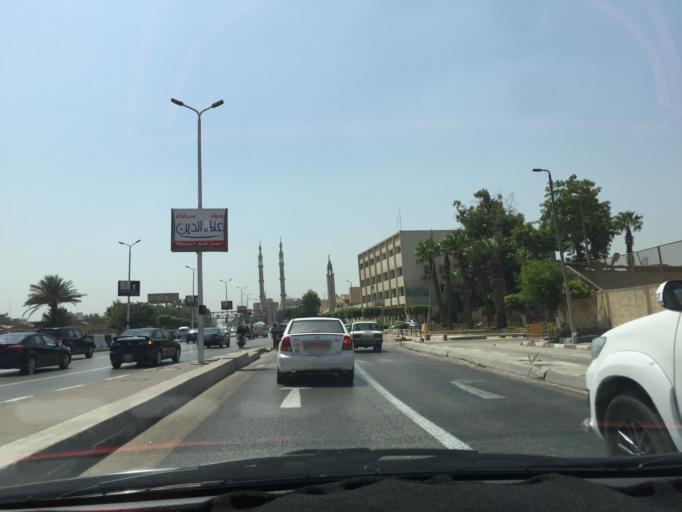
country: EG
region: Muhafazat al Qahirah
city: Cairo
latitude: 30.0652
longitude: 31.2876
